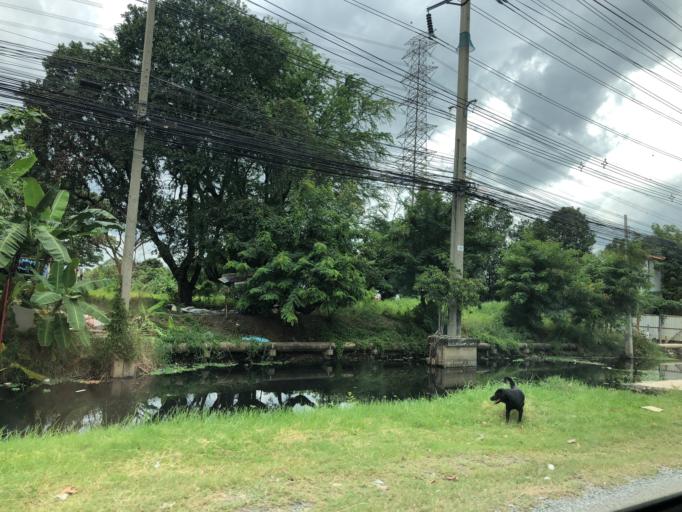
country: TH
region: Bangkok
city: Lak Si
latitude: 13.8861
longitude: 100.5521
